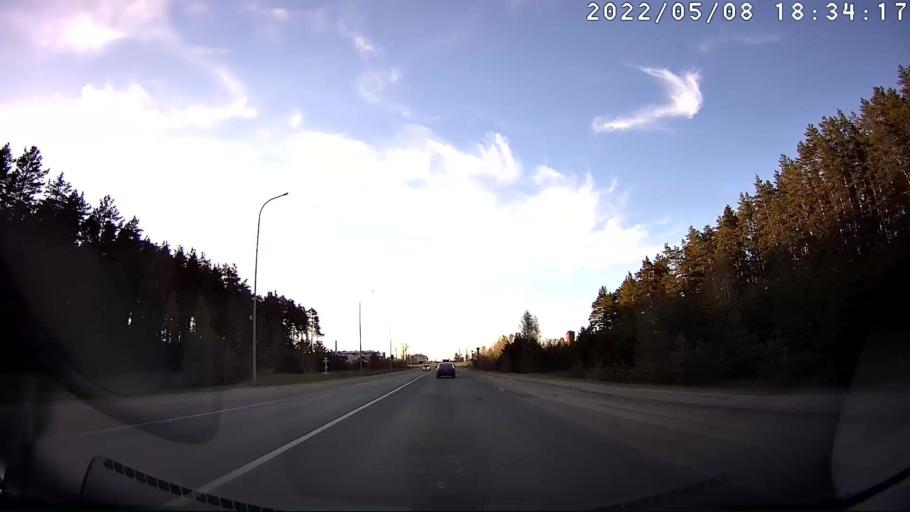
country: RU
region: Mariy-El
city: Volzhsk
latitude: 55.8989
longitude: 48.3563
